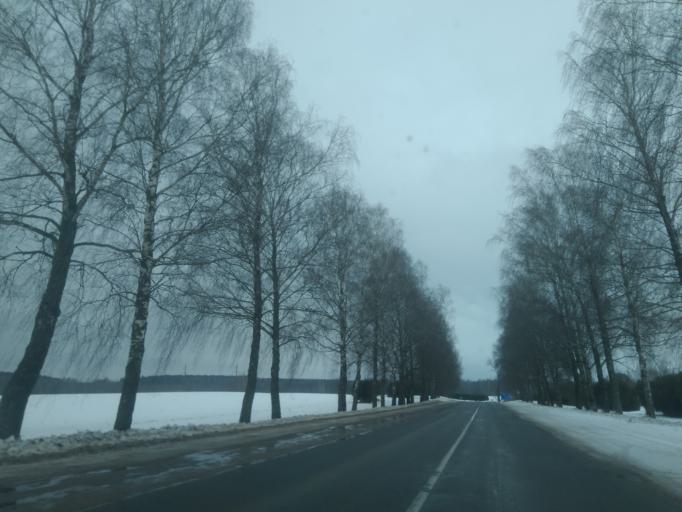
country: BY
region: Minsk
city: Ivyanyets
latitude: 53.9028
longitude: 26.7572
